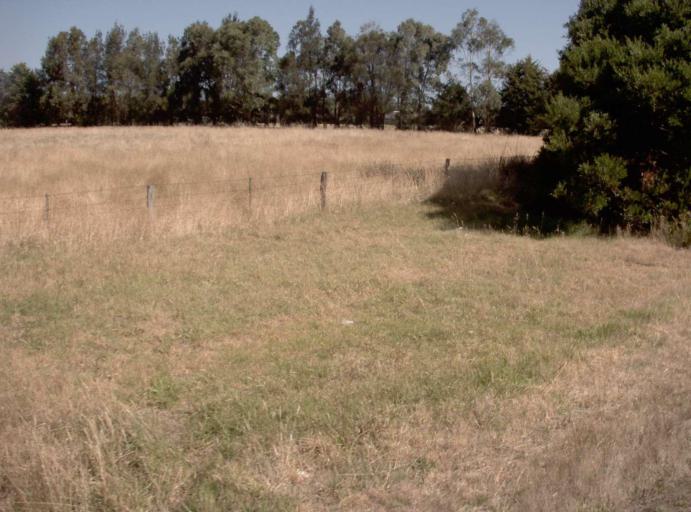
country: AU
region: Victoria
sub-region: Frankston
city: Carrum Downs
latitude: -38.0836
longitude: 145.1854
